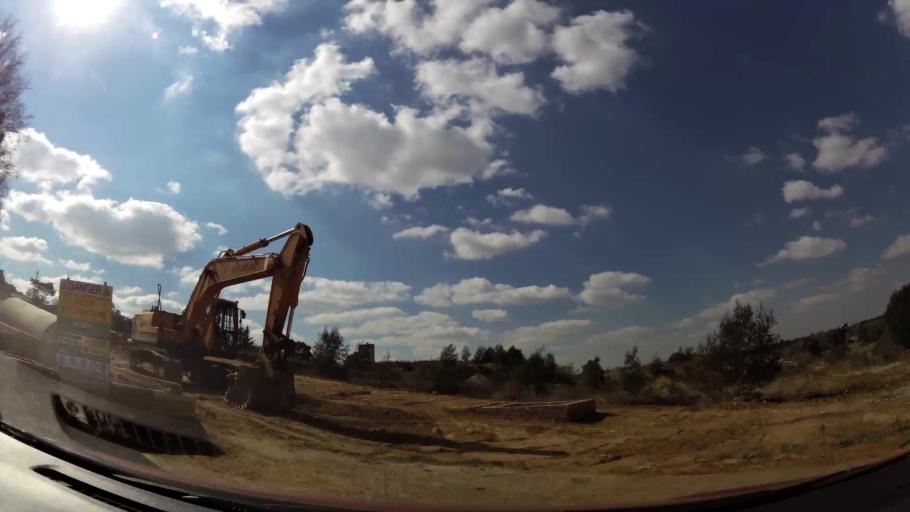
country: ZA
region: Gauteng
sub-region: West Rand District Municipality
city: Muldersdriseloop
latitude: -26.0693
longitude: 27.9653
